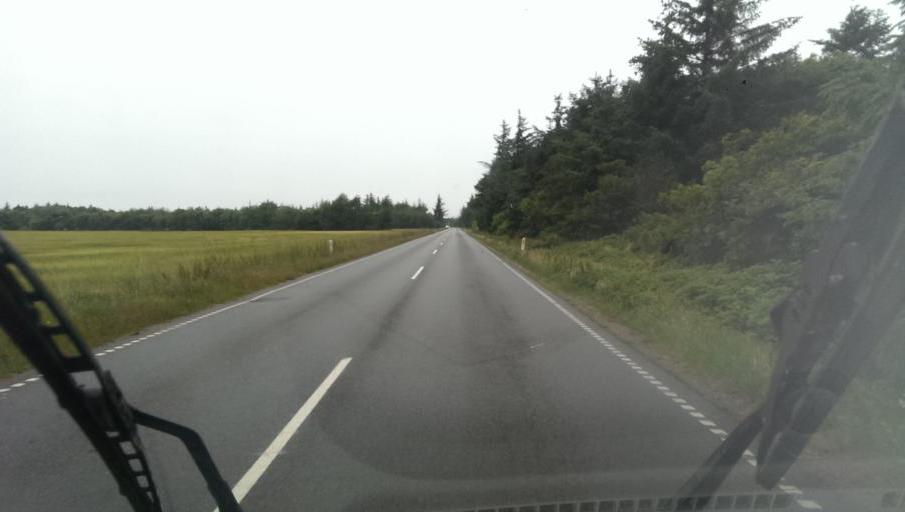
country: DK
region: South Denmark
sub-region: Varde Kommune
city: Oksbol
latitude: 55.8096
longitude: 8.2189
